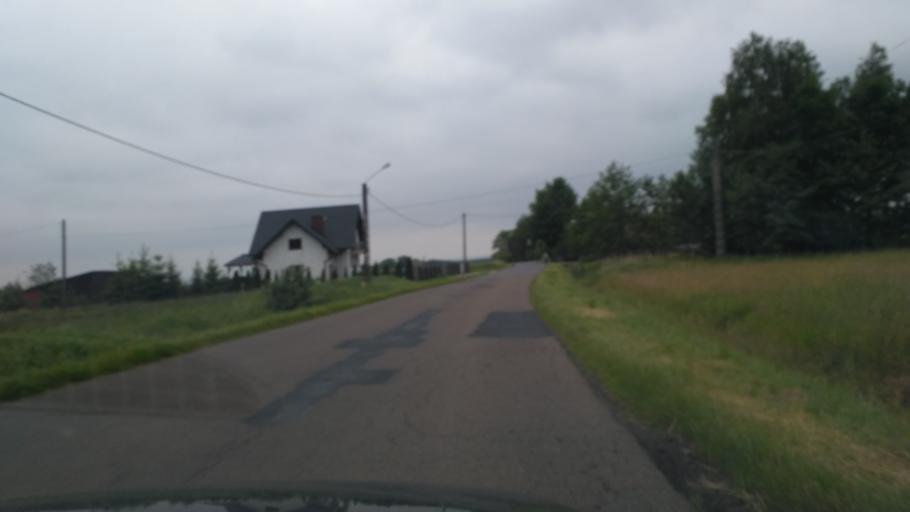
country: PL
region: Subcarpathian Voivodeship
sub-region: Powiat kolbuszowski
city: Niwiska
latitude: 50.1650
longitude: 21.6691
